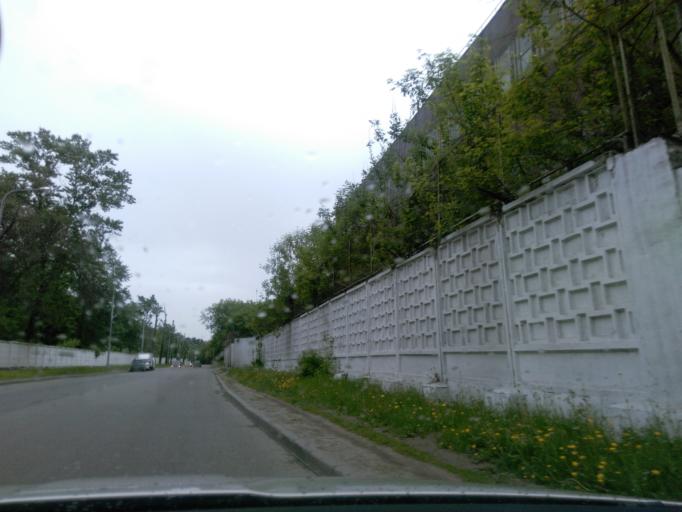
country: RU
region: Moscow
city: Taganskiy
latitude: 55.7321
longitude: 37.6874
